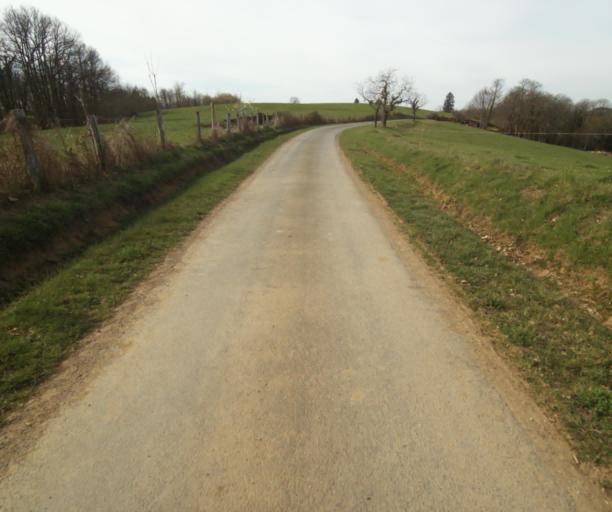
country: FR
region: Limousin
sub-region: Departement de la Correze
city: Correze
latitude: 45.4128
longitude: 1.8067
